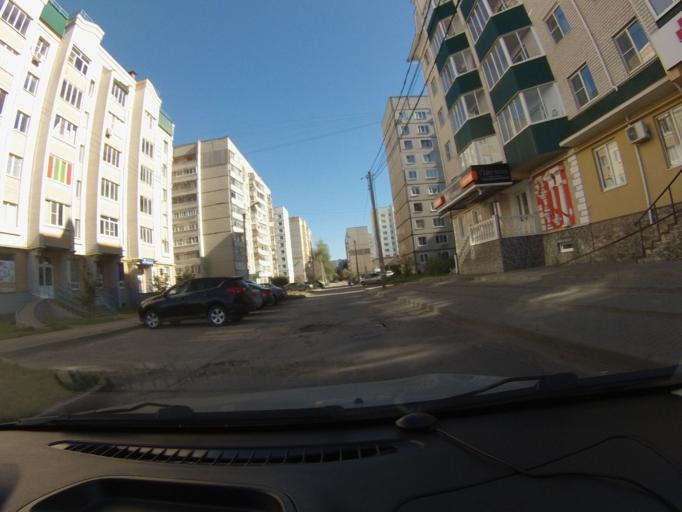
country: RU
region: Tambov
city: Tambov
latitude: 52.7705
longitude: 41.4090
